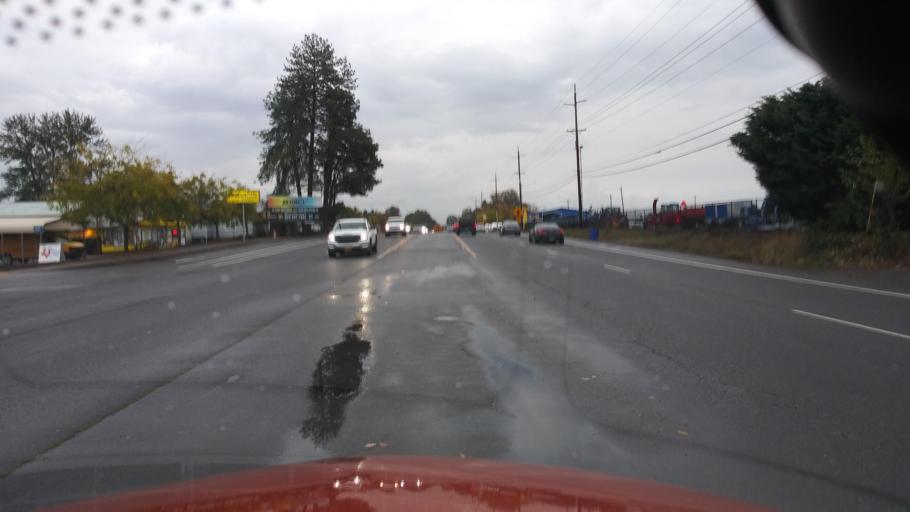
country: US
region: Oregon
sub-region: Washington County
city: Cornelius
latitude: 45.5200
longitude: -123.0361
